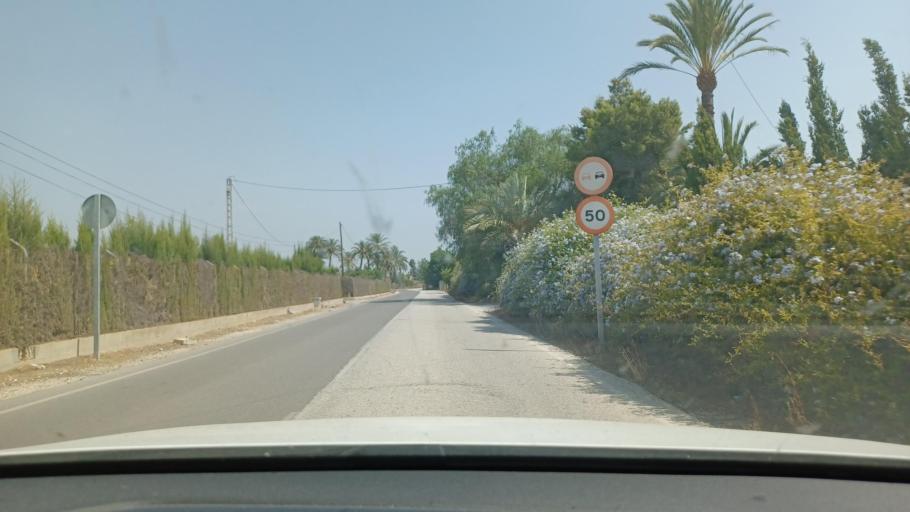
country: ES
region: Valencia
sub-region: Provincia de Alicante
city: Elche
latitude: 38.2330
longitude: -0.6934
